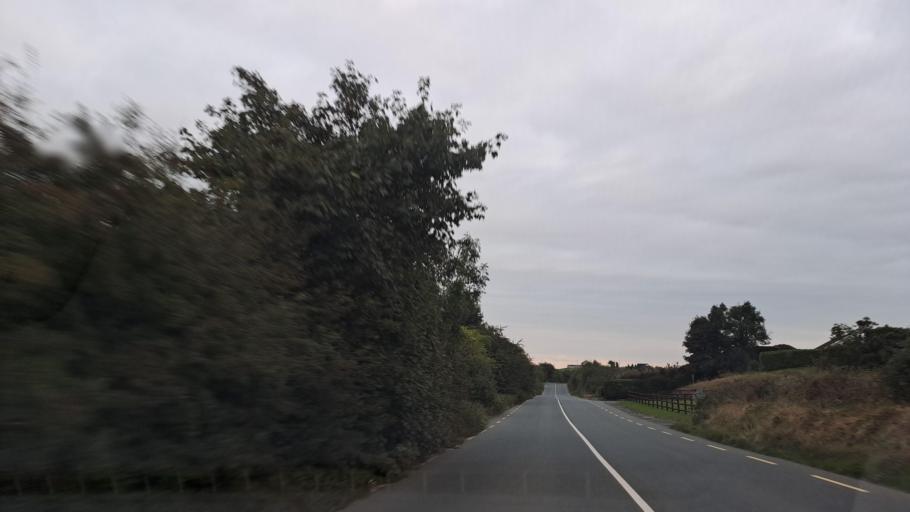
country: IE
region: Ulster
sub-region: County Monaghan
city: Carrickmacross
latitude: 54.0319
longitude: -6.7788
